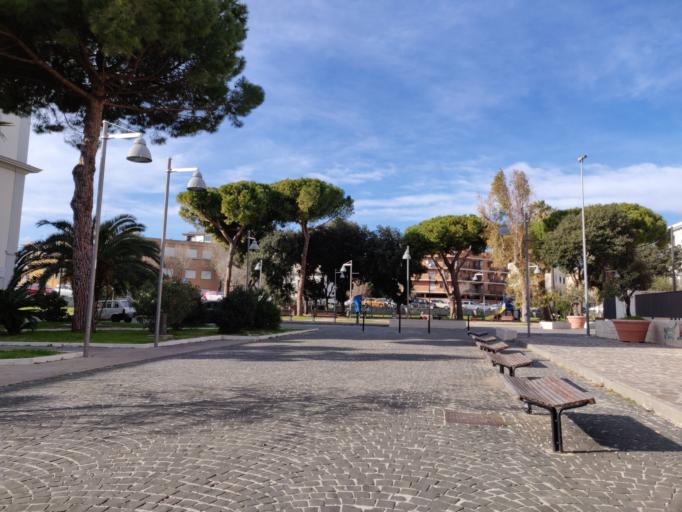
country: IT
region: Latium
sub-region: Citta metropolitana di Roma Capitale
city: Civitavecchia
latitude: 42.0911
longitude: 11.7969
